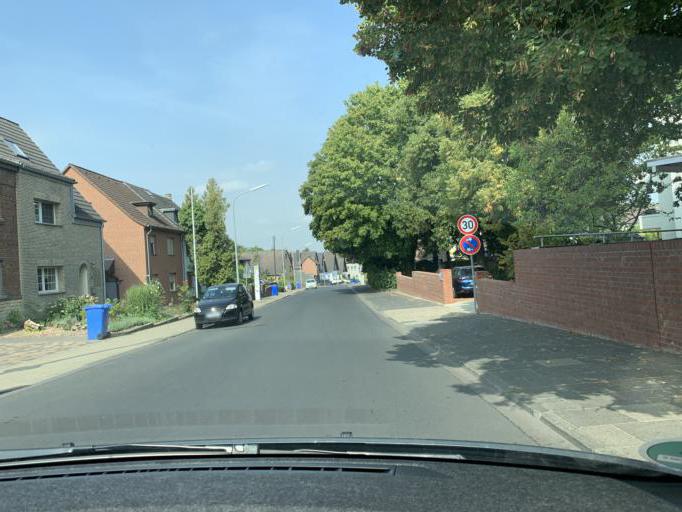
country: DE
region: North Rhine-Westphalia
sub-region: Regierungsbezirk Koln
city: Erftstadt
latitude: 50.8056
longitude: 6.8307
